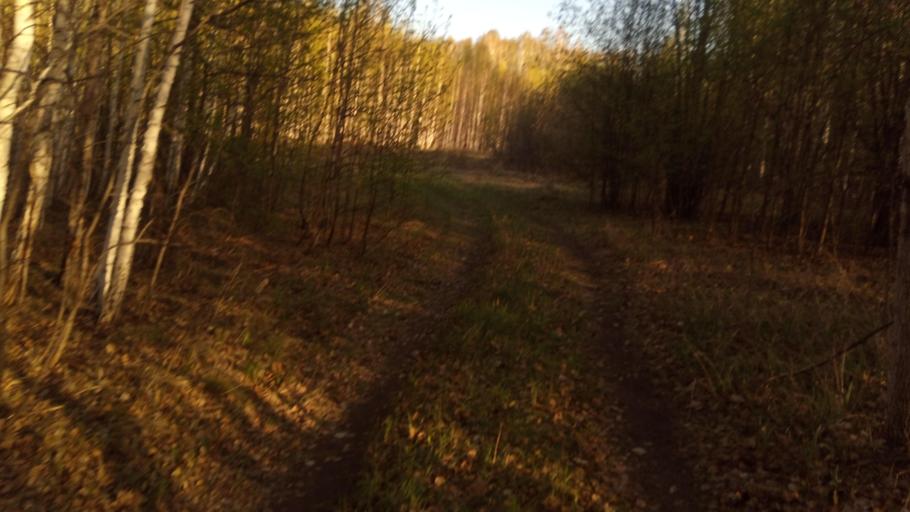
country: RU
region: Chelyabinsk
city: Timiryazevskiy
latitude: 54.9933
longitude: 60.8587
